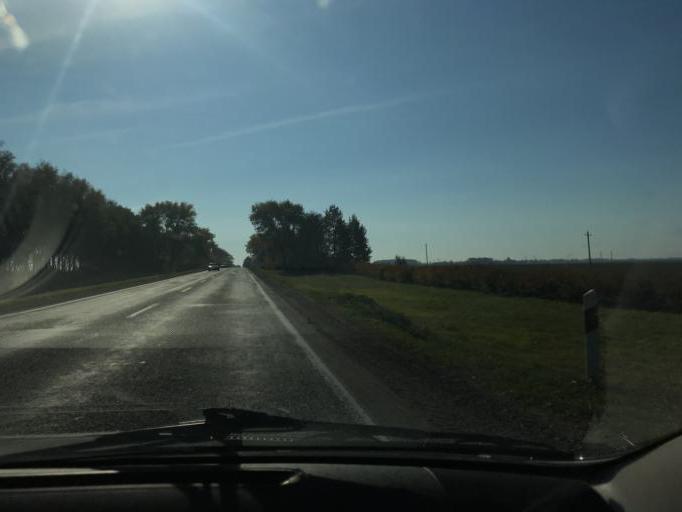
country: BY
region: Minsk
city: Salihorsk
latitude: 52.8422
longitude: 27.4662
